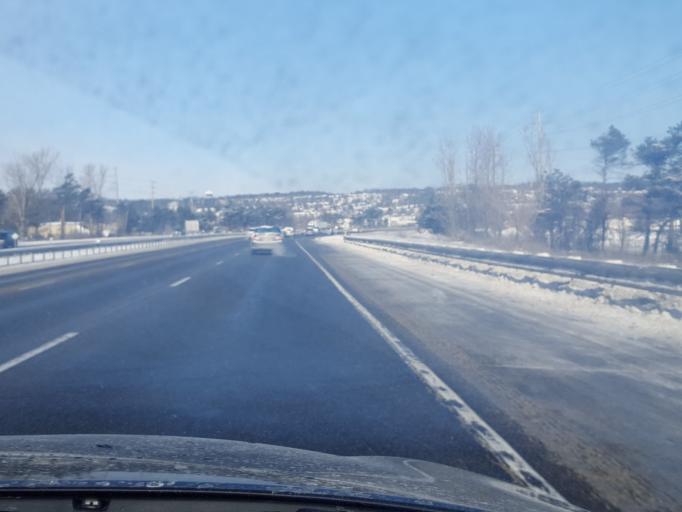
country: CA
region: Ontario
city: Barrie
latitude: 44.3718
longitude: -79.7084
